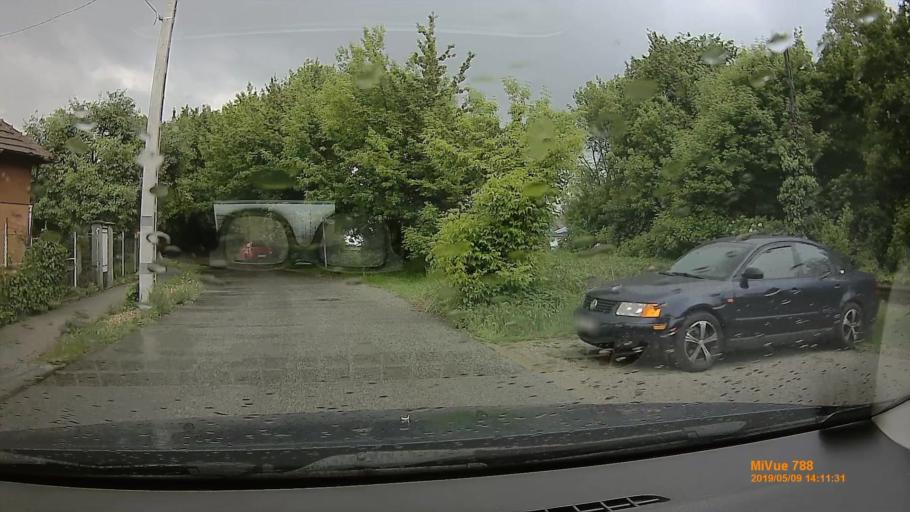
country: HU
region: Budapest
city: Budapest XVI. keruelet
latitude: 47.5086
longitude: 19.1738
